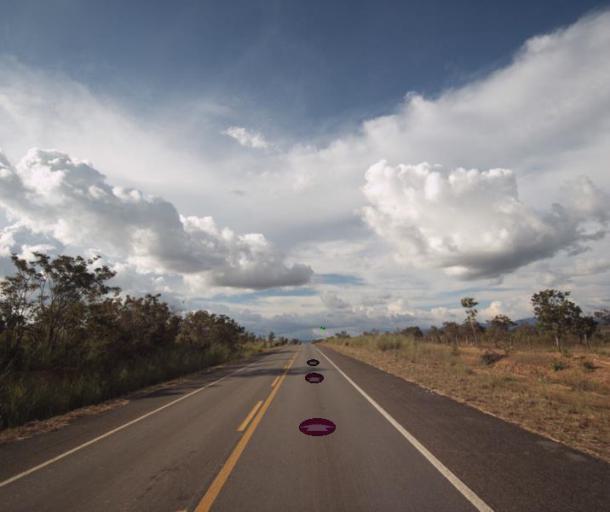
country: BR
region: Goias
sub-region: Barro Alto
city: Barro Alto
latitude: -14.8202
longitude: -48.6377
